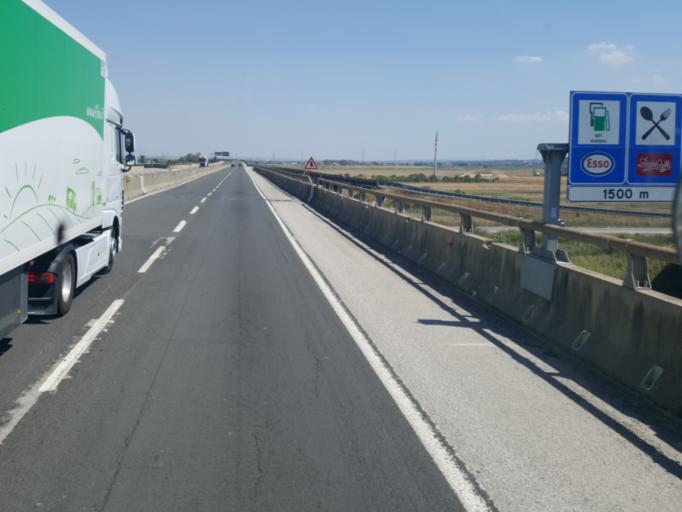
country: IT
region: Tuscany
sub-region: Provincia di Livorno
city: Guasticce
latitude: 43.6095
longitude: 10.4057
